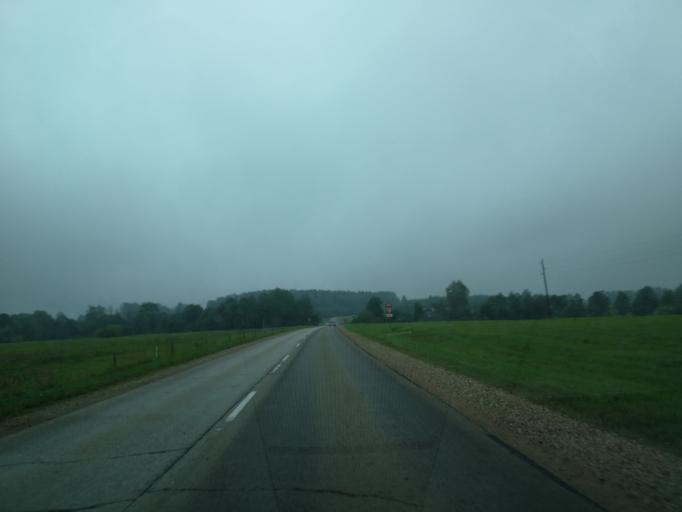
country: LV
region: Preilu Rajons
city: Preili
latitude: 56.2983
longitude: 26.6586
